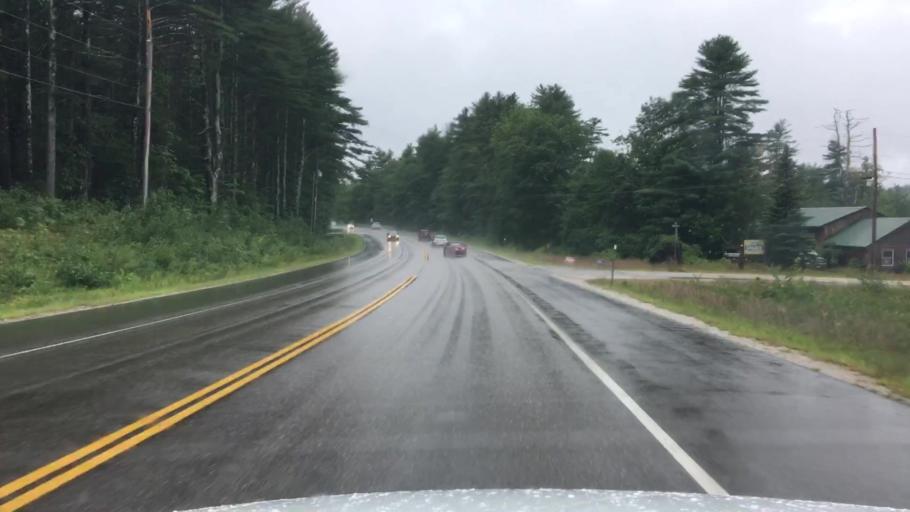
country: US
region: New Hampshire
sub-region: Carroll County
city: Conway
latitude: 43.9965
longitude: -71.0763
